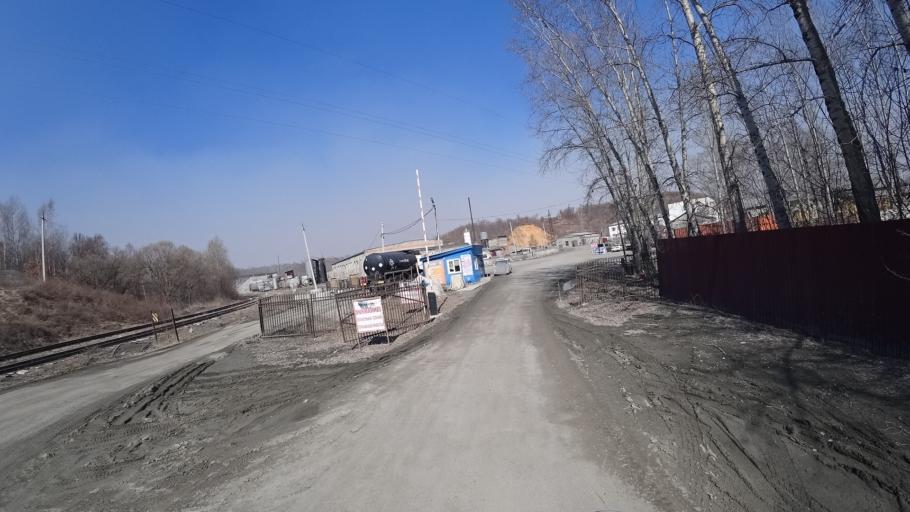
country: RU
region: Amur
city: Novobureyskiy
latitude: 49.7896
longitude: 129.9599
